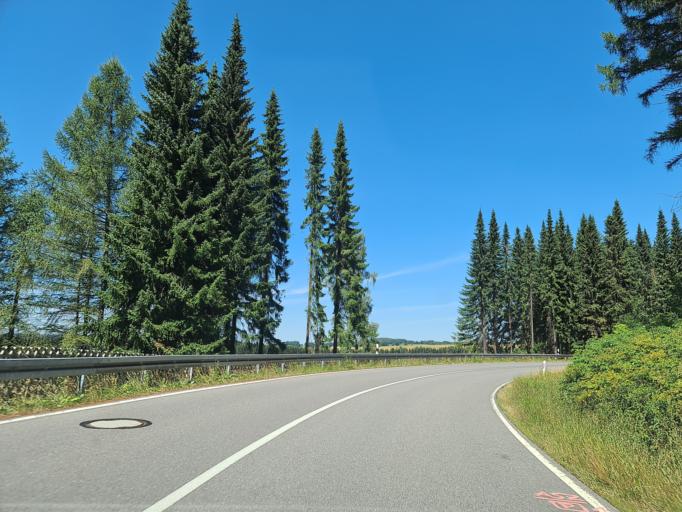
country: DE
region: Saxony
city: Neuhausen
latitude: 50.6929
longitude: 13.5029
